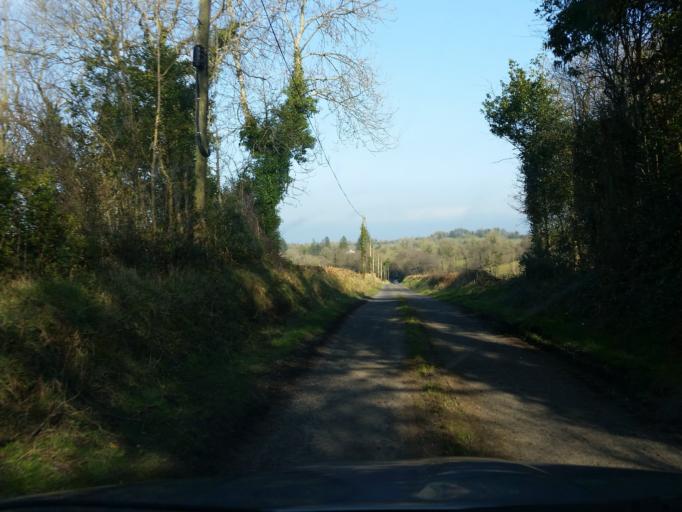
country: IE
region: Ulster
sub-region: County Monaghan
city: Clones
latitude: 54.2262
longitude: -7.2382
